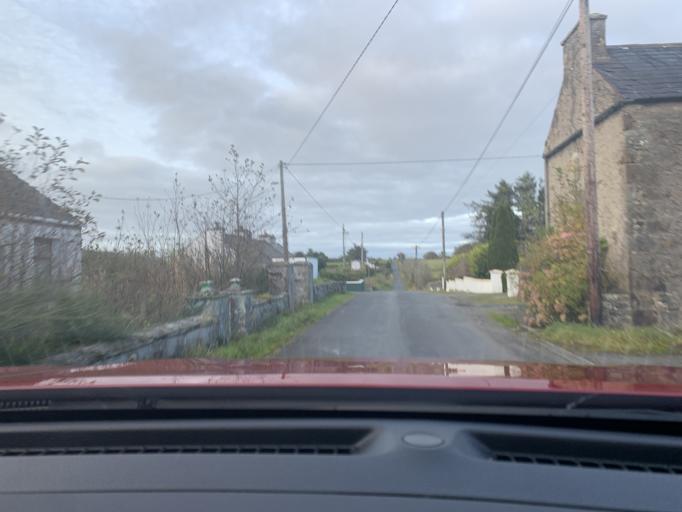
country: IE
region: Connaught
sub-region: Roscommon
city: Ballaghaderreen
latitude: 53.9752
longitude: -8.6207
